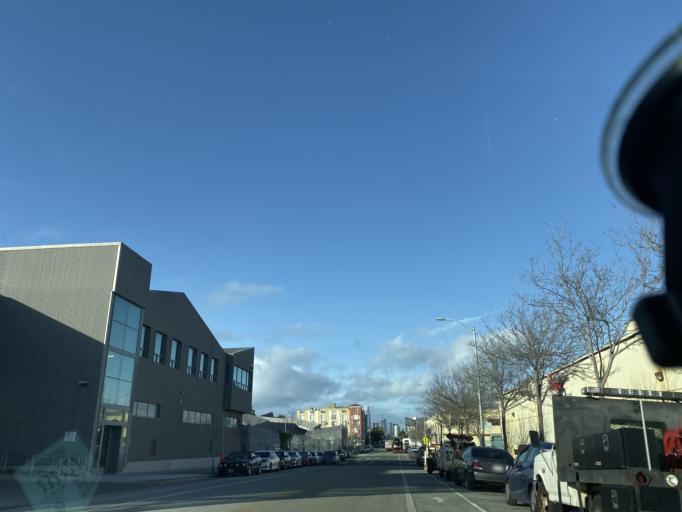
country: US
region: California
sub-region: San Francisco County
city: San Francisco
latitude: 37.7480
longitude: -122.3902
